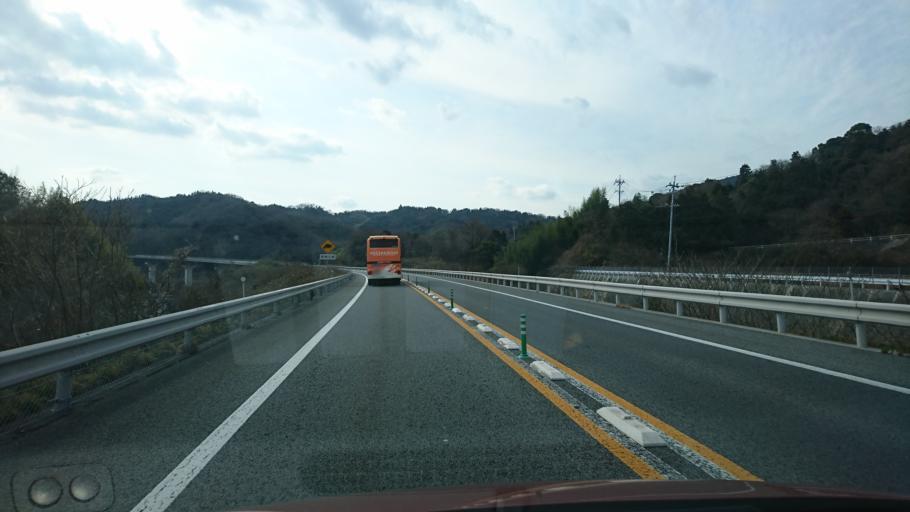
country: JP
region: Hiroshima
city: Innoshima
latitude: 34.1704
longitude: 133.0653
